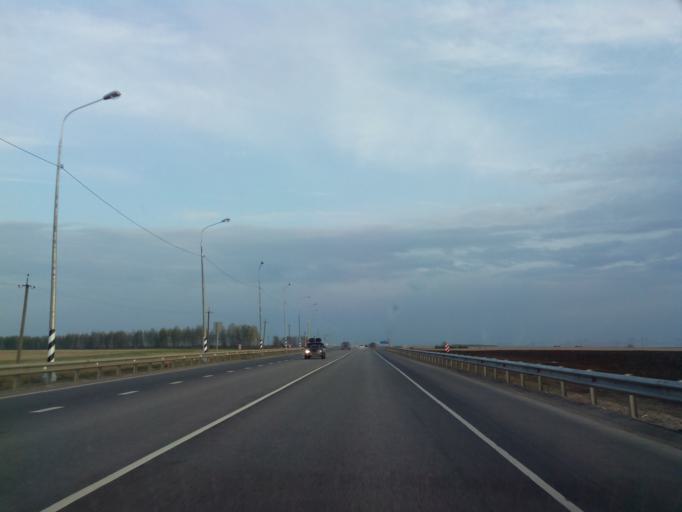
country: RU
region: Rjazan
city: Ryazhsk
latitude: 53.5825
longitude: 40.0415
